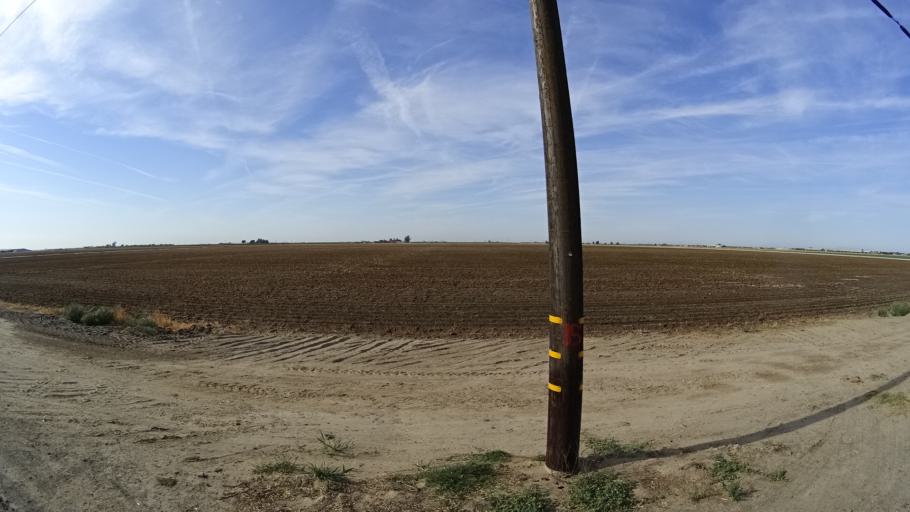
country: US
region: California
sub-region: Fresno County
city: Kingsburg
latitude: 36.4160
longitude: -119.5487
